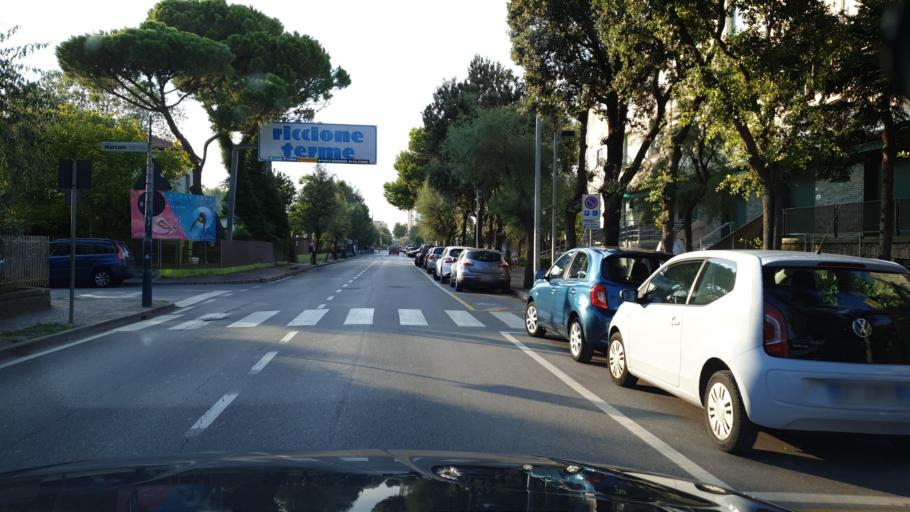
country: IT
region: Emilia-Romagna
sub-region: Provincia di Rimini
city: Riccione
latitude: 43.9941
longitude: 12.6741
